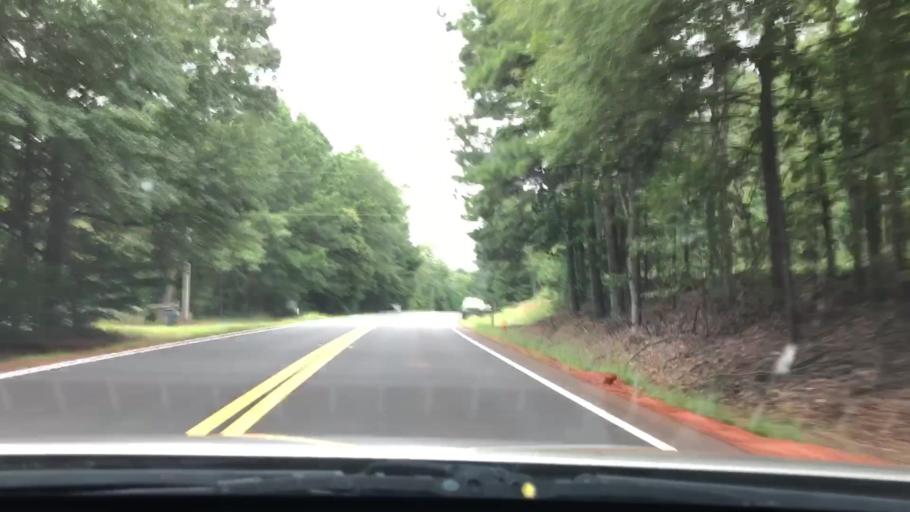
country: US
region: Georgia
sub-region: Upson County
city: Hannahs Mill
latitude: 33.0156
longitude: -84.4126
